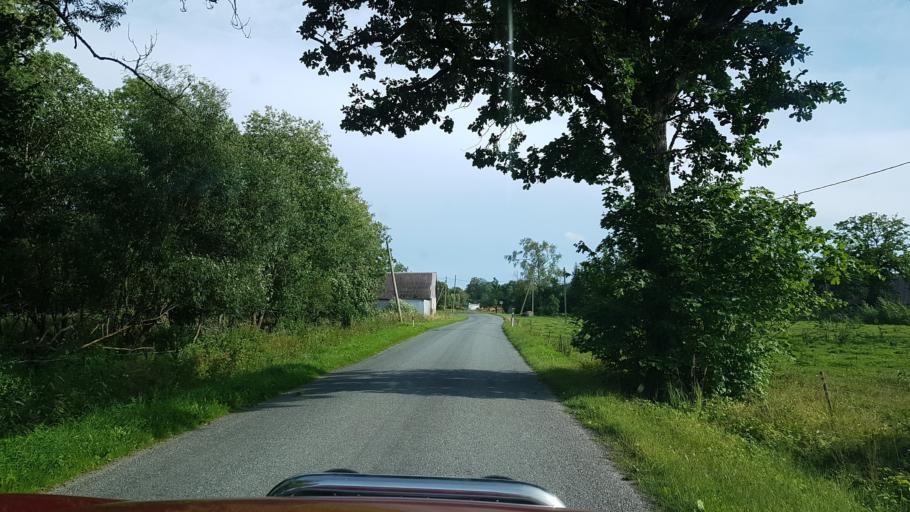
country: EE
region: Laeaene
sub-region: Lihula vald
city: Lihula
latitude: 58.4501
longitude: 23.9970
